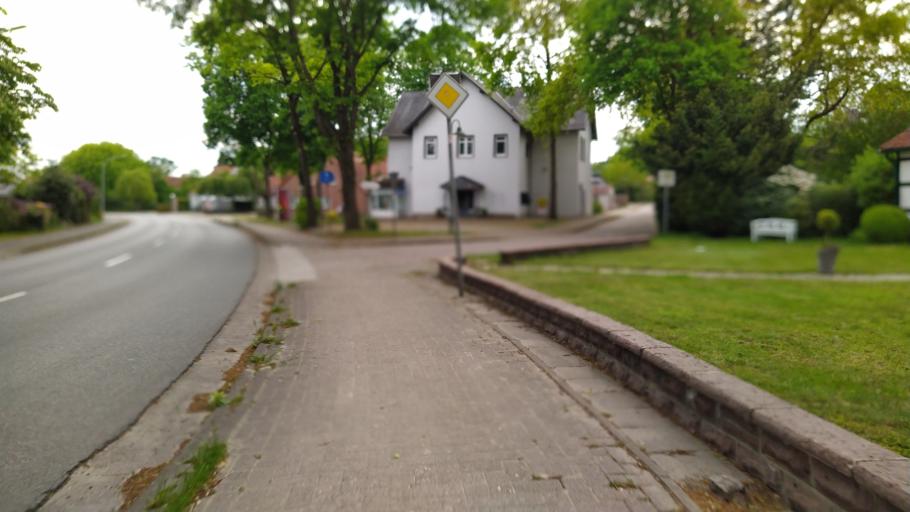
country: DE
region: Lower Saxony
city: Tarmstedt
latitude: 53.2267
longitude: 9.0779
